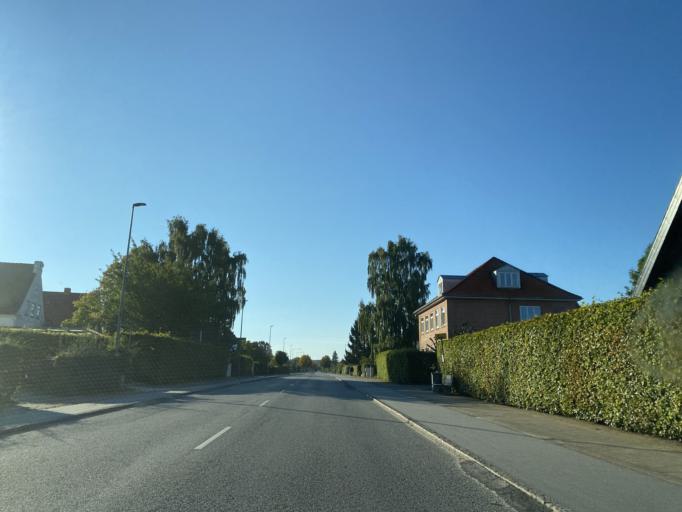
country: DK
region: South Denmark
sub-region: Haderslev Kommune
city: Haderslev
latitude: 55.2429
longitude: 9.4901
